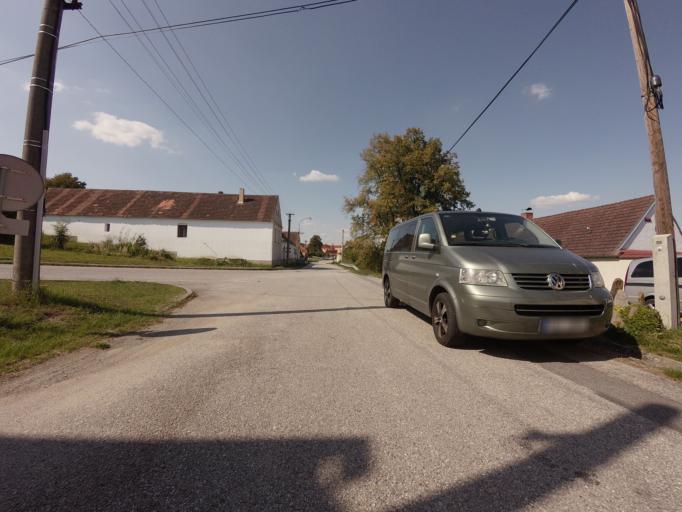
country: CZ
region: Jihocesky
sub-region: Okres Ceske Budejovice
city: Hluboka nad Vltavou
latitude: 49.1270
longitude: 14.4527
